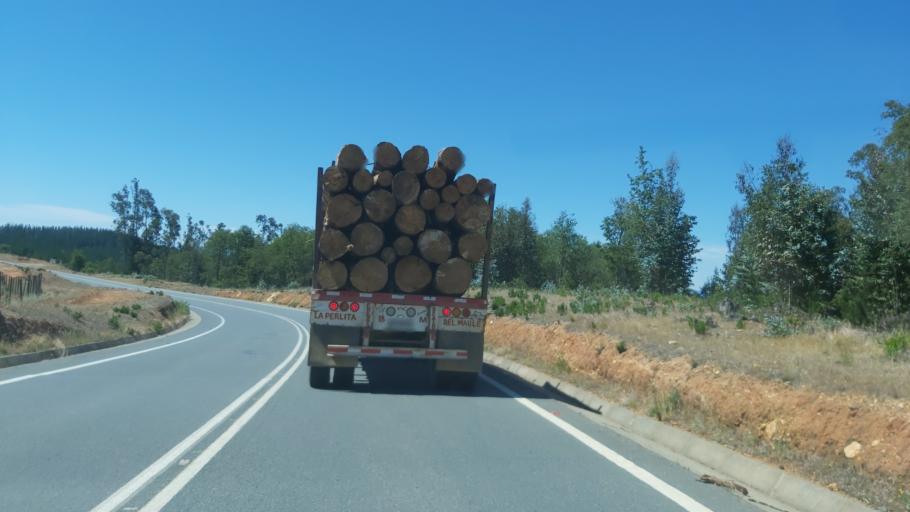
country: CL
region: Maule
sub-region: Provincia de Talca
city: Talca
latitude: -34.9449
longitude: -71.9763
